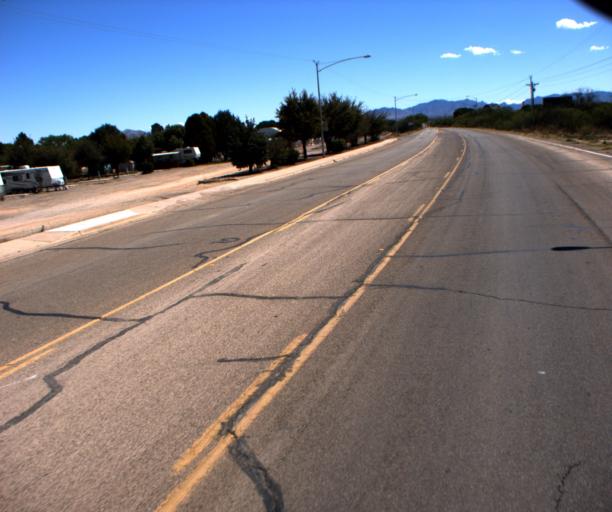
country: US
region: Arizona
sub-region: Cochise County
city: Benson
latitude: 31.9651
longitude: -110.2836
